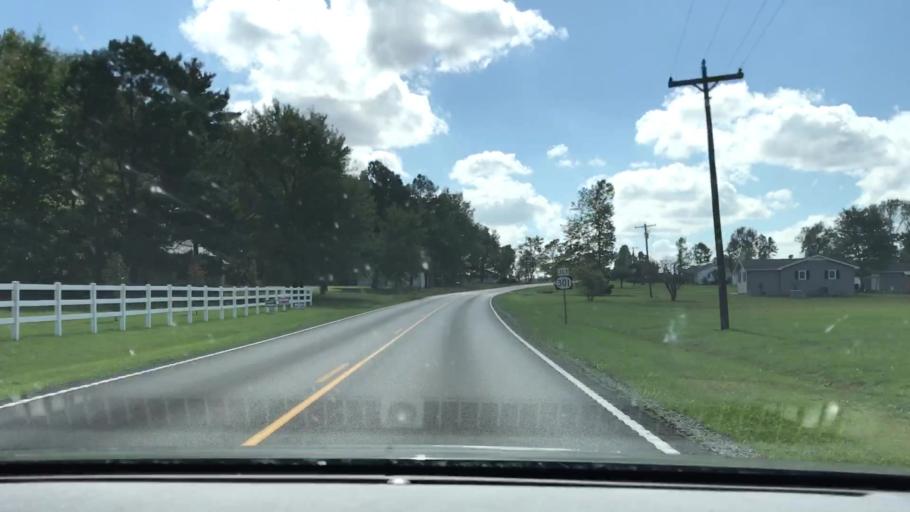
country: US
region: Kentucky
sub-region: Graves County
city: Mayfield
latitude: 36.8576
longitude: -88.5716
